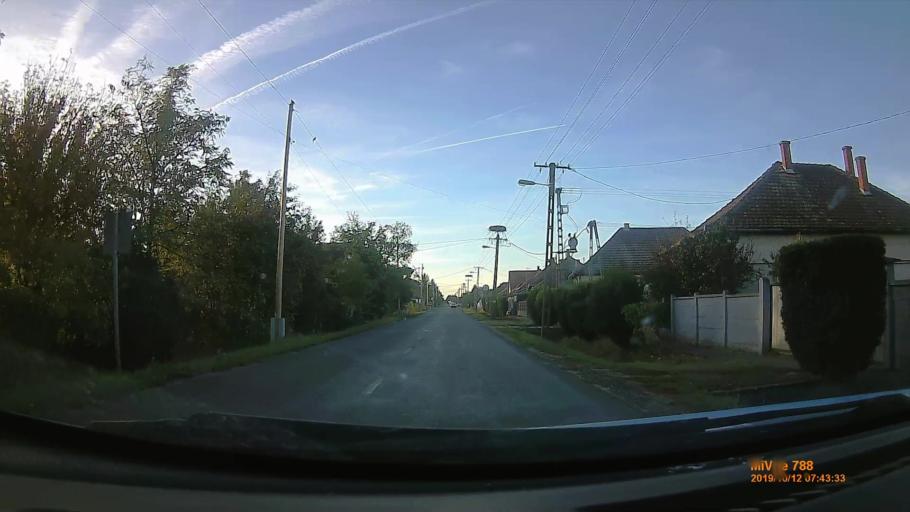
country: RO
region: Bihor
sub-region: Comuna Bors
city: Bors
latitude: 47.1927
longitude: 21.7876
